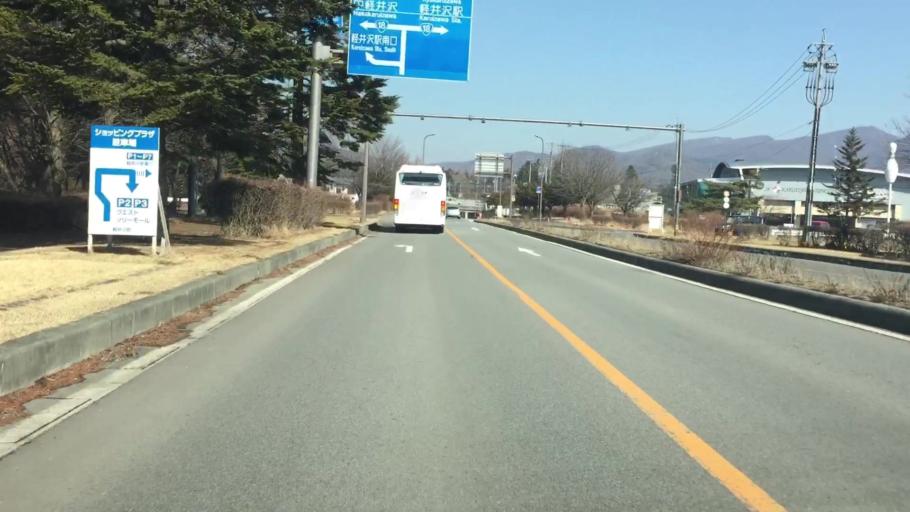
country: JP
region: Nagano
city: Saku
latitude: 36.3408
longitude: 138.6307
